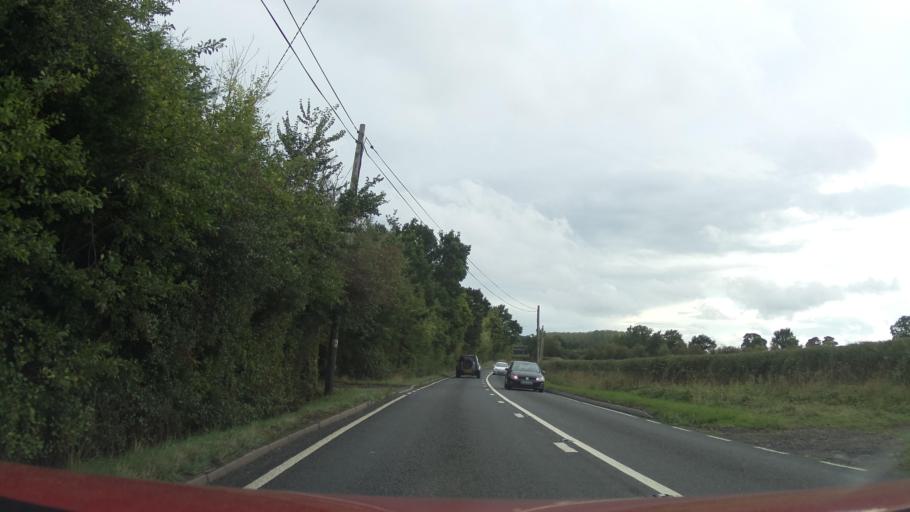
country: GB
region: England
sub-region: Worcestershire
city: Droitwich
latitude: 52.3025
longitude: -2.1747
